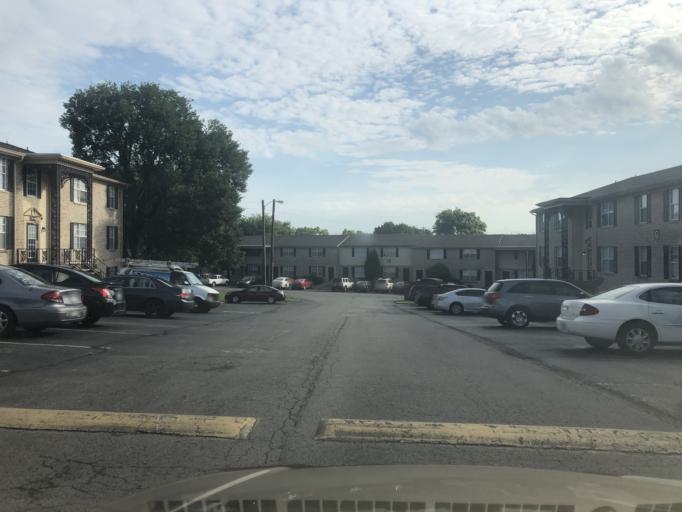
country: US
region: Tennessee
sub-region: Davidson County
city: Goodlettsville
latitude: 36.2457
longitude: -86.7141
